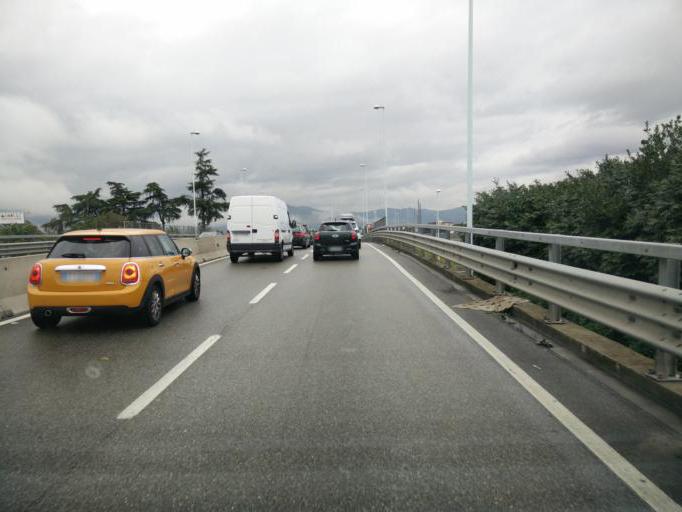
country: IT
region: Tuscany
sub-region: Provincia di Prato
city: Prato
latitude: 43.8771
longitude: 11.0626
